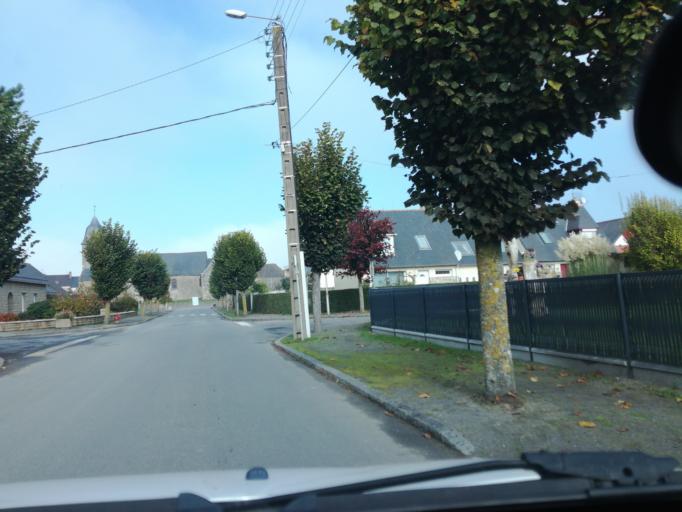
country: FR
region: Brittany
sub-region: Departement d'Ille-et-Vilaine
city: Cherrueix
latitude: 48.6040
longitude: -1.7105
